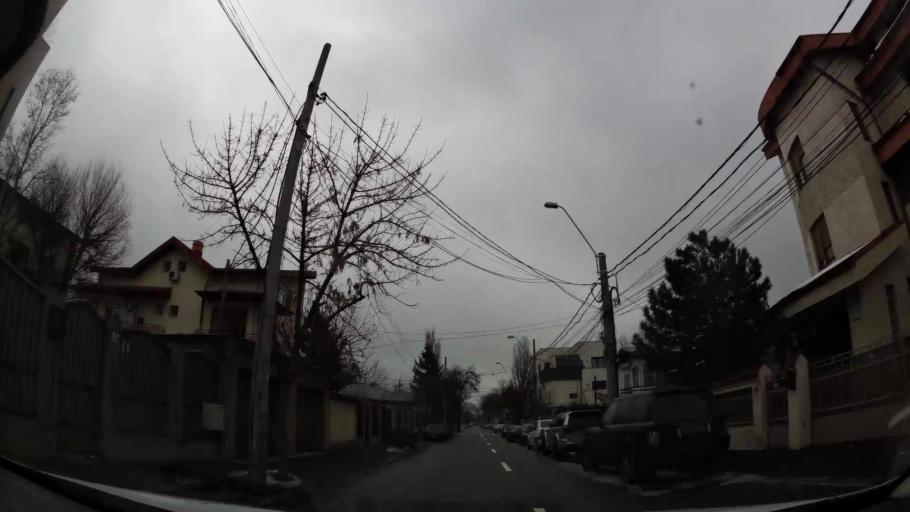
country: RO
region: Ilfov
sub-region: Comuna Chiajna
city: Rosu
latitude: 44.4903
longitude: 26.0296
